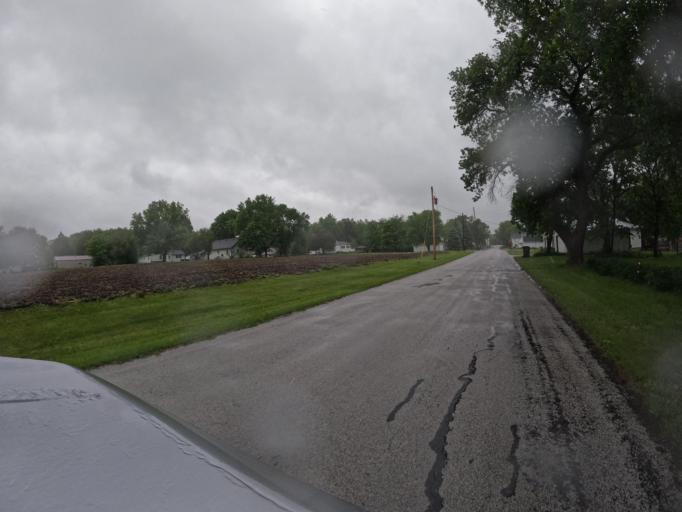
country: US
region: Nebraska
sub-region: Gage County
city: Wymore
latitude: 40.1370
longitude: -96.6598
